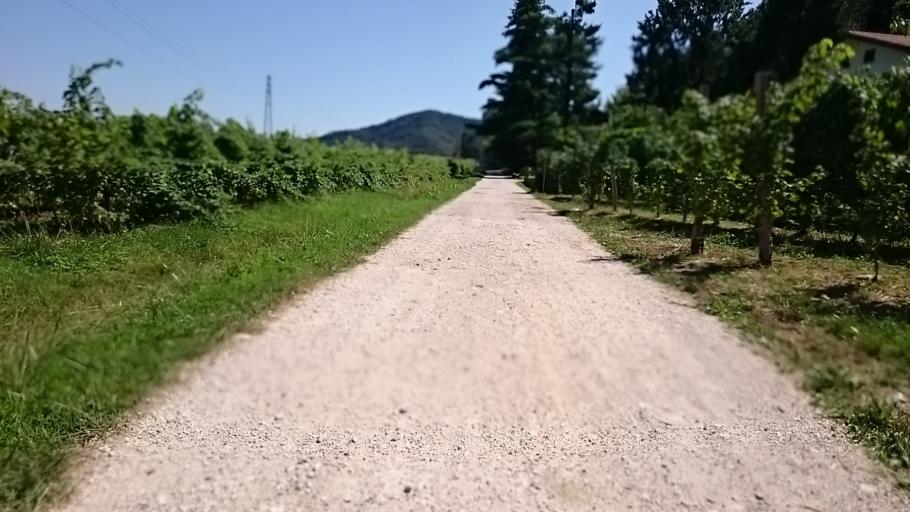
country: IT
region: Veneto
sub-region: Provincia di Treviso
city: Follina
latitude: 45.9434
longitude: 12.1247
